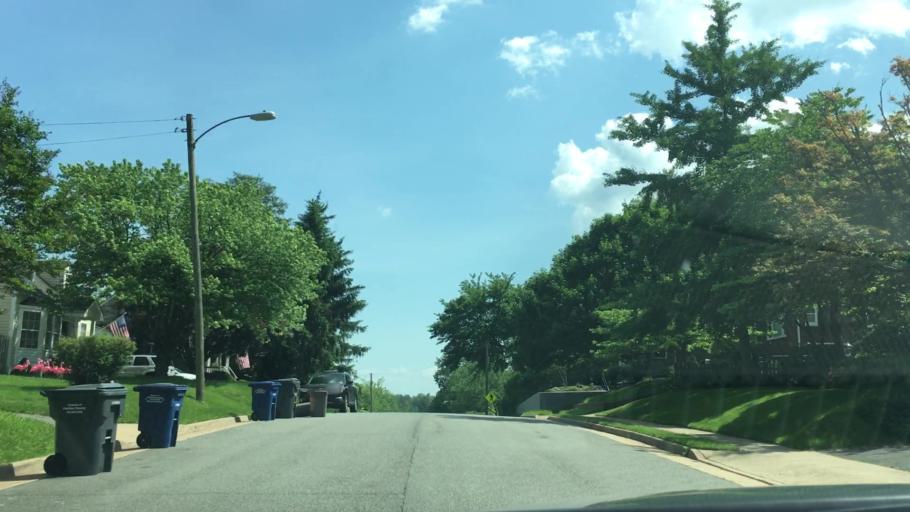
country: US
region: Virginia
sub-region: City of Falls Church
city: Falls Church
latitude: 38.8768
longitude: -77.1803
